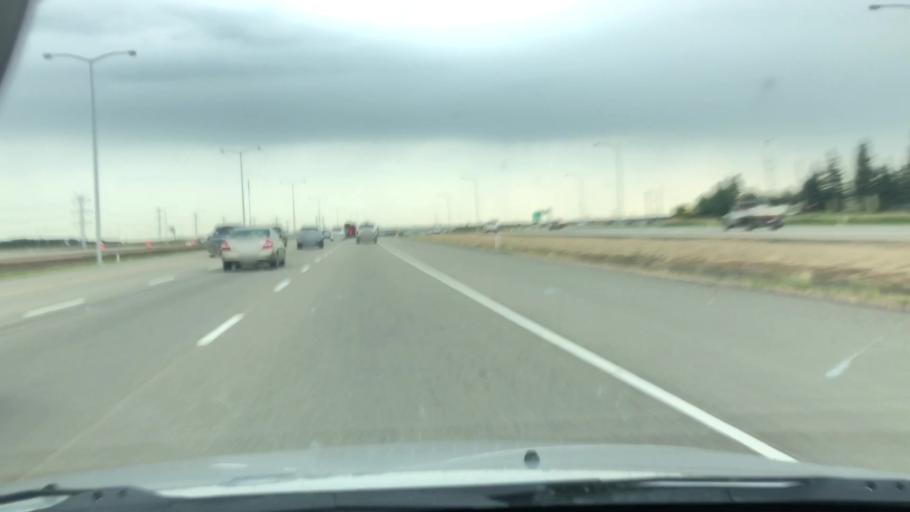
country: CA
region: Alberta
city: Sherwood Park
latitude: 53.4887
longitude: -113.3435
